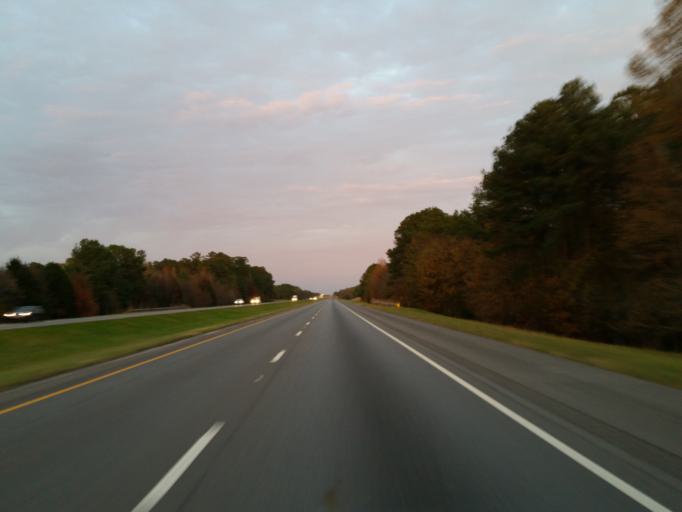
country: US
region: Alabama
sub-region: Sumter County
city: Livingston
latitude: 32.7226
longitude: -88.1171
